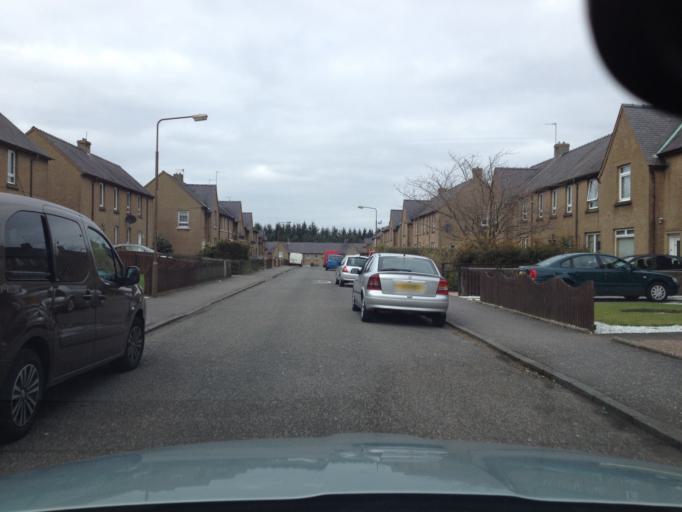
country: GB
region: Scotland
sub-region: West Lothian
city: Livingston
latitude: 55.9161
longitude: -3.5053
